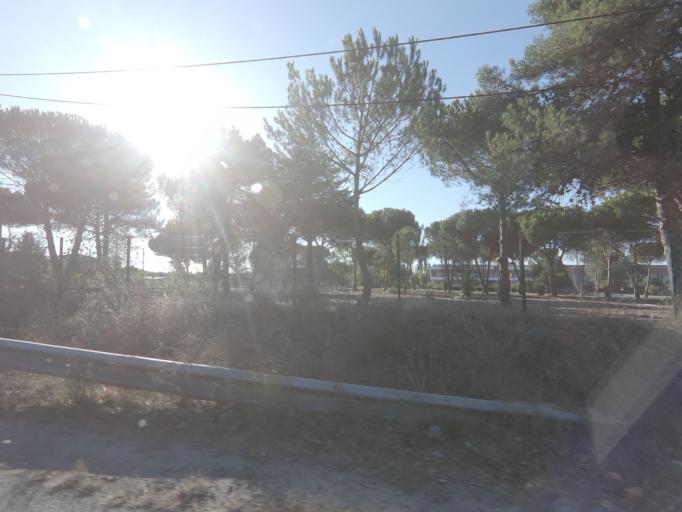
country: PT
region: Setubal
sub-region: Palmela
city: Quinta do Anjo
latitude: 38.5275
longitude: -8.9949
